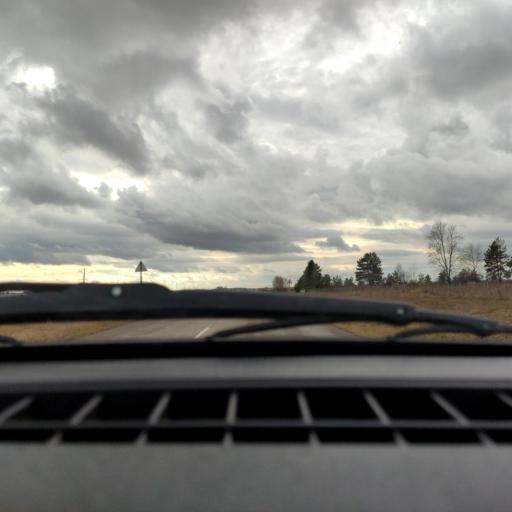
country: RU
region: Bashkortostan
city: Asanovo
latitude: 54.9267
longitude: 55.5157
